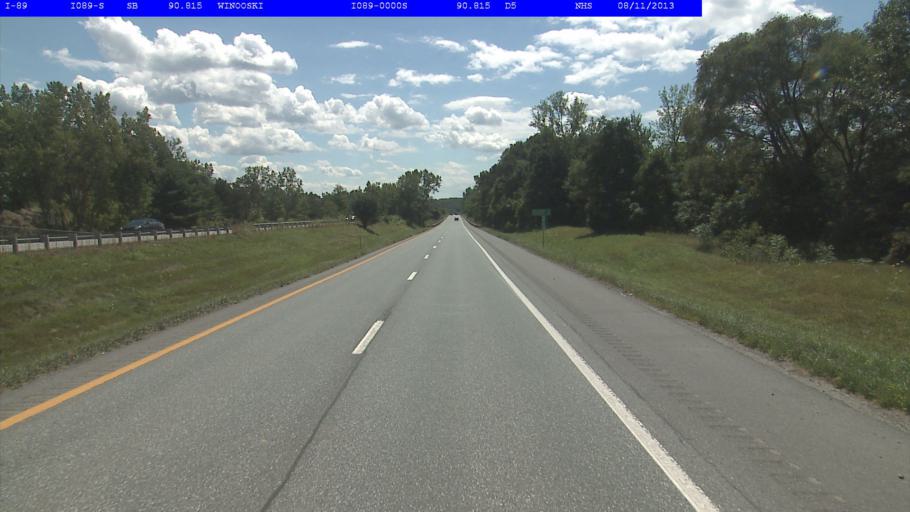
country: US
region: Vermont
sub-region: Chittenden County
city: Winooski
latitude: 44.4982
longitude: -73.1738
